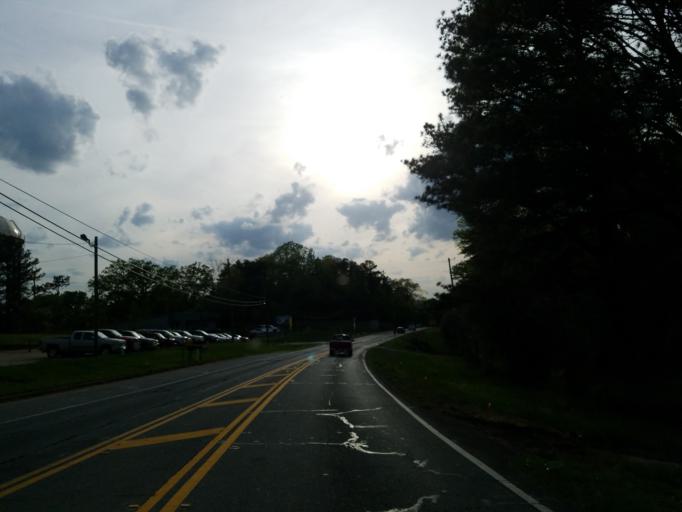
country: US
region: Georgia
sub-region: Cherokee County
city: Canton
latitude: 34.2347
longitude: -84.4450
